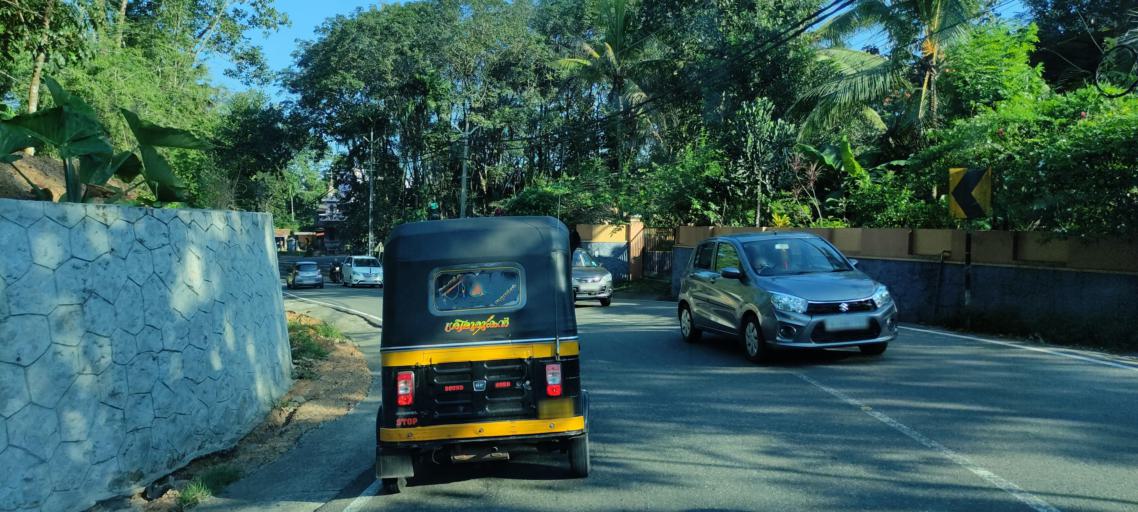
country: IN
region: Kerala
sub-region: Pattanamtitta
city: Adur
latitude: 9.1657
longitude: 76.7417
